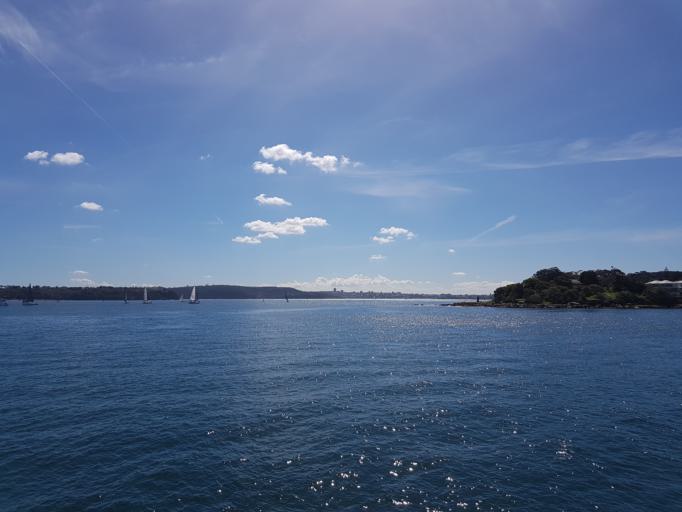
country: AU
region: New South Wales
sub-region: Waverley
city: Dover Heights
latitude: -33.8441
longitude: 151.2757
